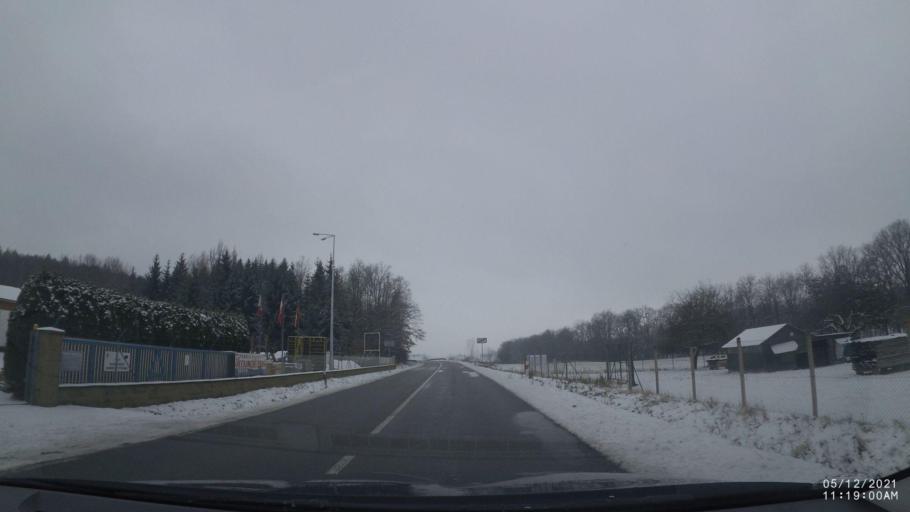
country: CZ
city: Solnice
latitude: 50.1943
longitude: 16.2298
